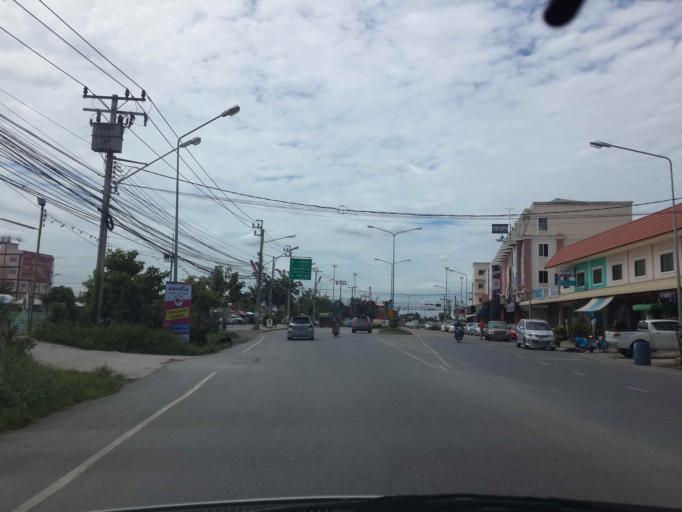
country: TH
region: Bangkok
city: Khan Na Yao
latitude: 13.8605
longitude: 100.6930
